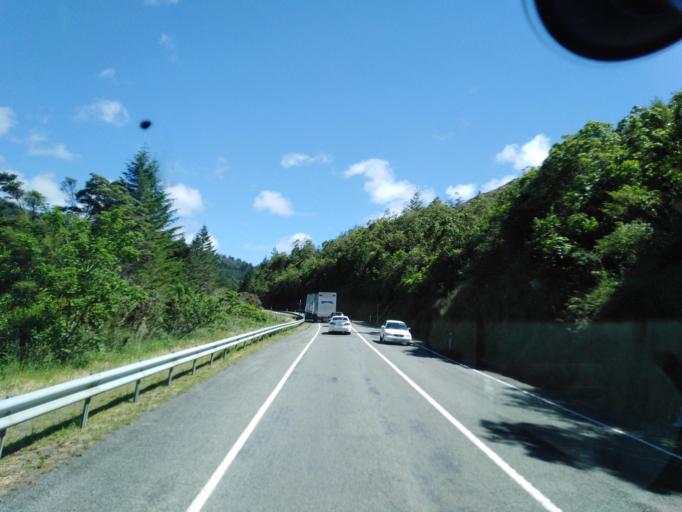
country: NZ
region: Nelson
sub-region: Nelson City
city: Nelson
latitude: -41.1985
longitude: 173.5605
